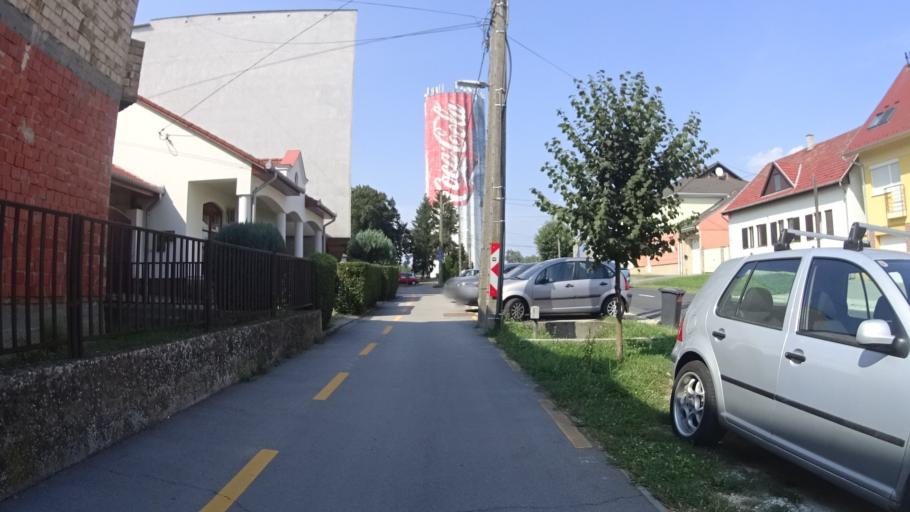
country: HU
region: Zala
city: Nagykanizsa
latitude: 46.4625
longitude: 16.9990
